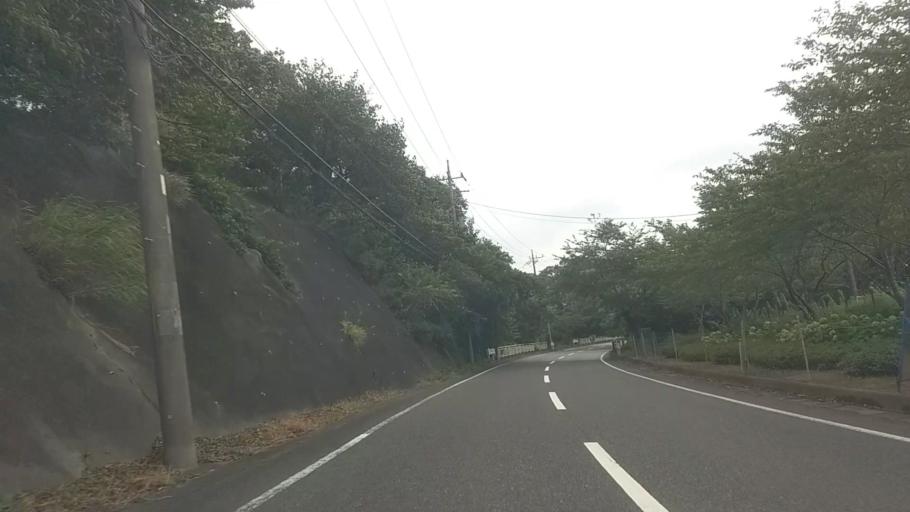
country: JP
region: Chiba
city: Kimitsu
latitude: 35.2253
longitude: 139.9544
